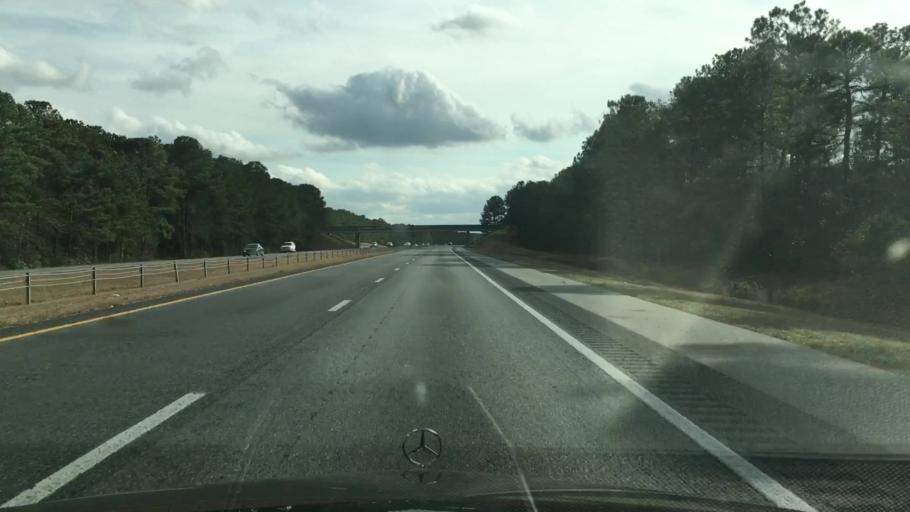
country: US
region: North Carolina
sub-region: Duplin County
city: Warsaw
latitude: 35.0522
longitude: -78.1558
